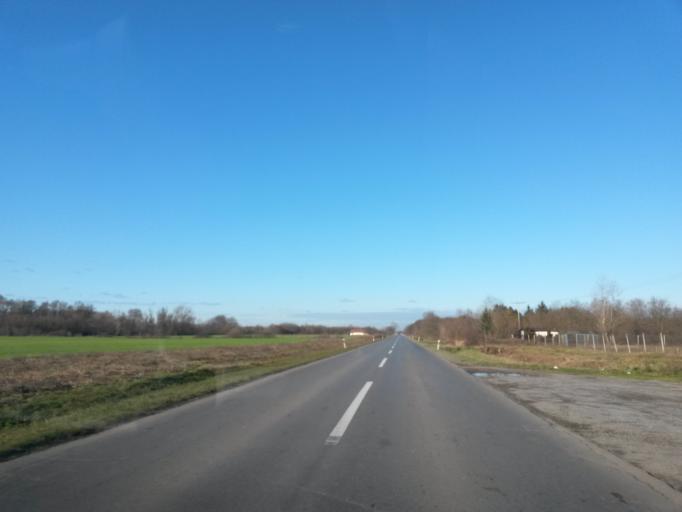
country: HR
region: Osjecko-Baranjska
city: Petrijevci
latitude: 45.6225
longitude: 18.5094
